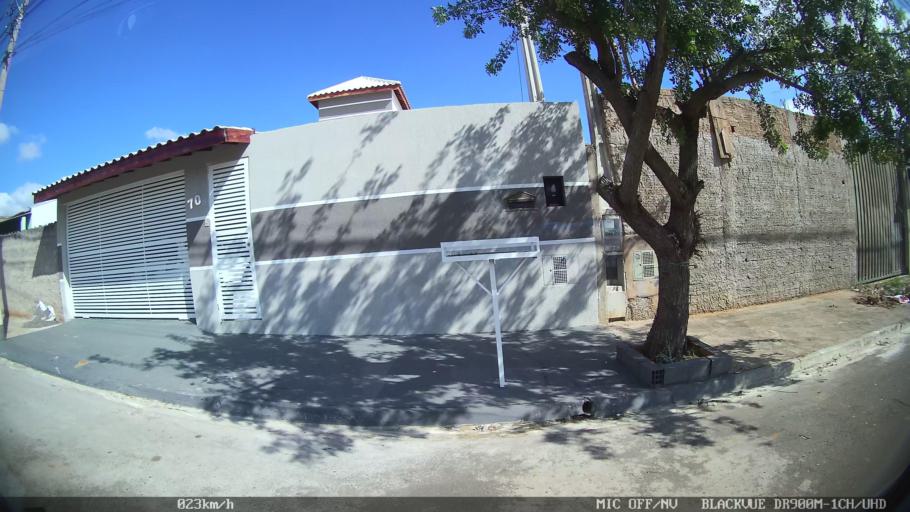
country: BR
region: Sao Paulo
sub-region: Hortolandia
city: Hortolandia
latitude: -22.8860
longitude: -47.2220
